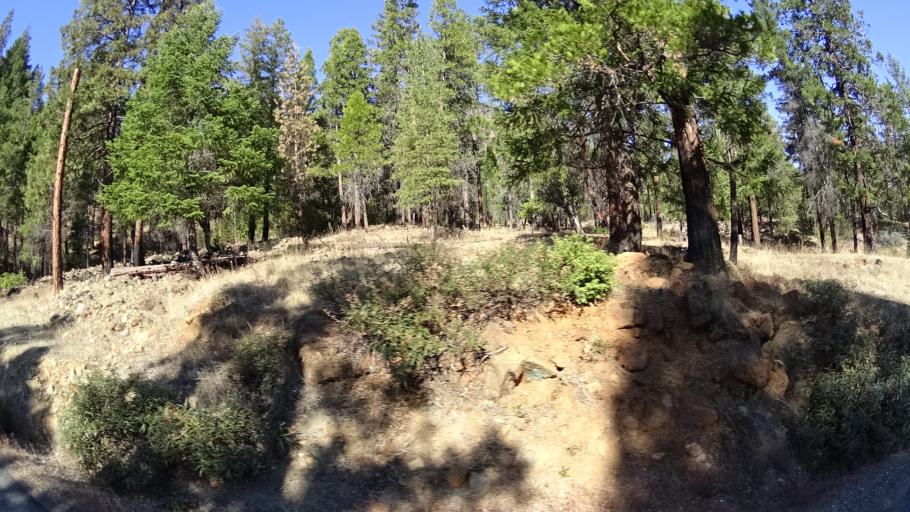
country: US
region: California
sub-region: Siskiyou County
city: Happy Camp
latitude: 41.7134
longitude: -123.0257
